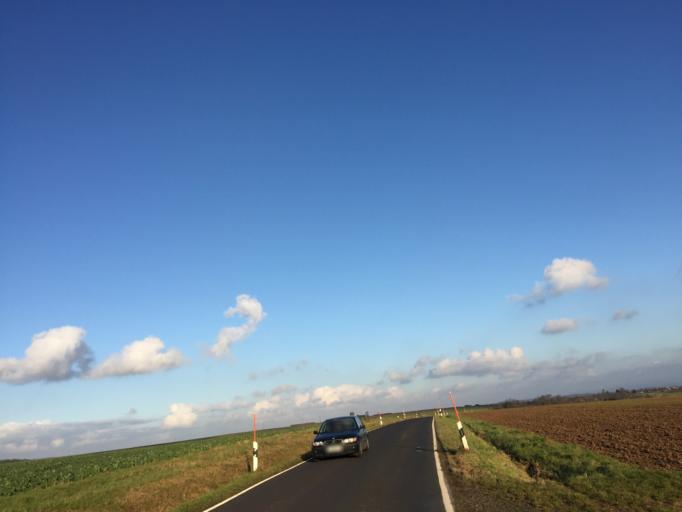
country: DE
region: Hesse
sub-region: Regierungsbezirk Giessen
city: Langgons
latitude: 50.5034
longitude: 8.7065
